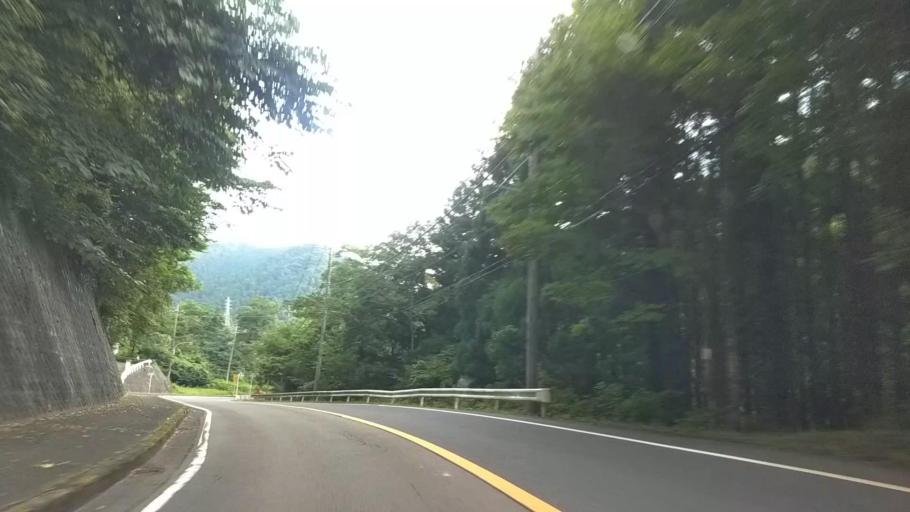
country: JP
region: Tokyo
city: Hachioji
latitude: 35.5614
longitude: 139.2360
